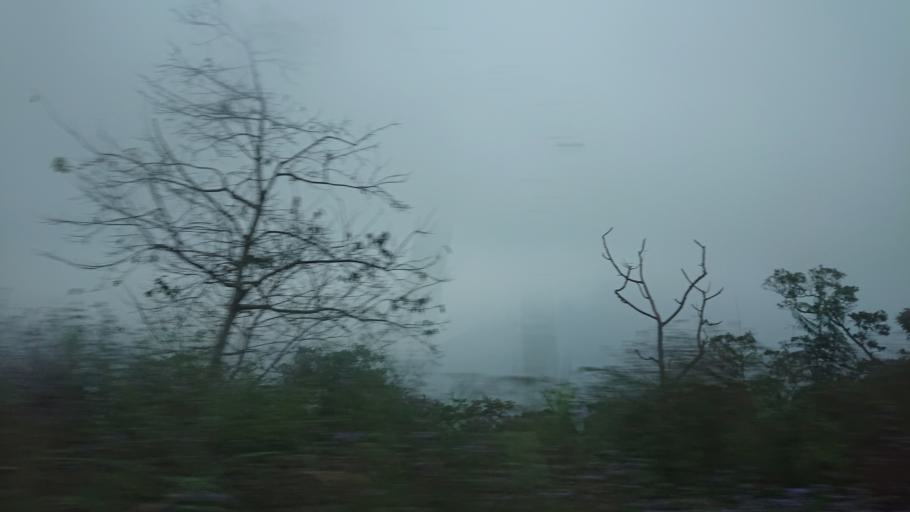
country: TW
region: Taiwan
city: Lugu
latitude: 23.5938
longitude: 120.7135
